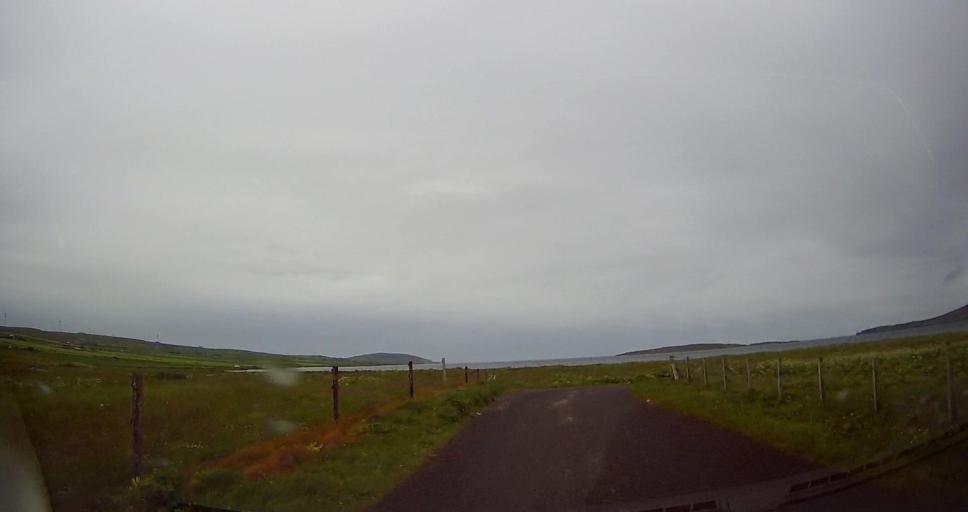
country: GB
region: Scotland
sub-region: Orkney Islands
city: Orkney
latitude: 59.1180
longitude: -3.0856
